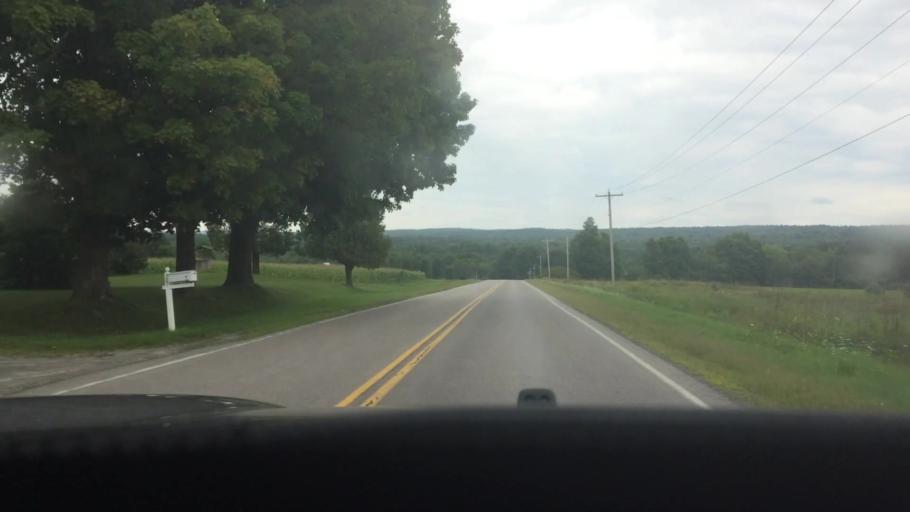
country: US
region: New York
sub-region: St. Lawrence County
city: Canton
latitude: 44.5404
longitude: -75.0816
